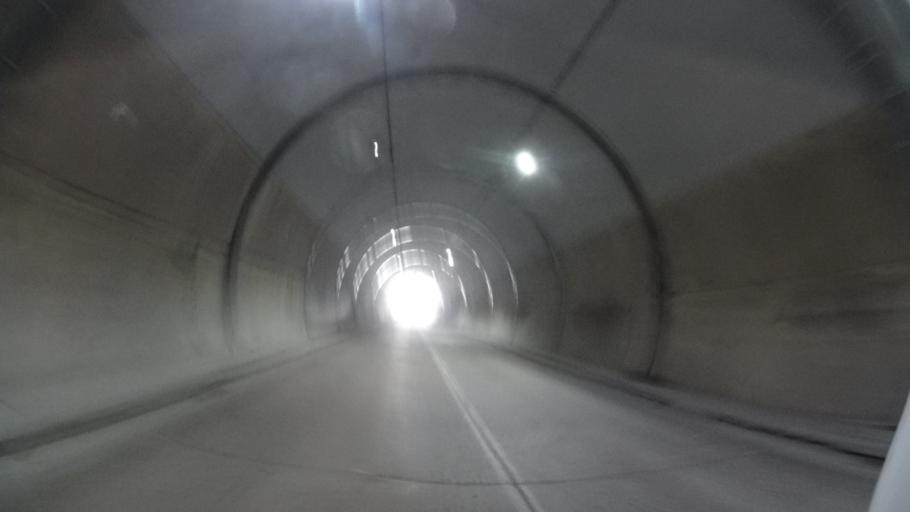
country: JP
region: Fukui
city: Ono
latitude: 35.9933
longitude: 136.3605
